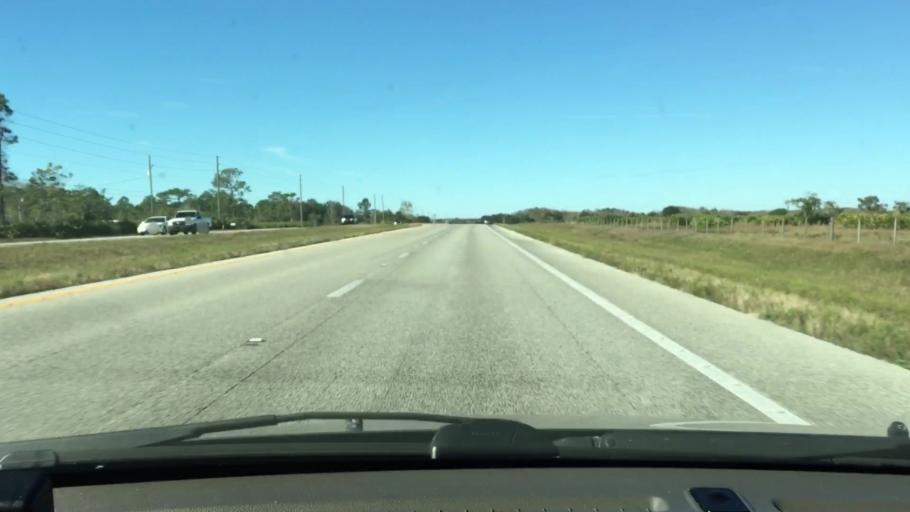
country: US
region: Florida
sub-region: Brevard County
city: June Park
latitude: 28.1259
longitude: -80.9736
